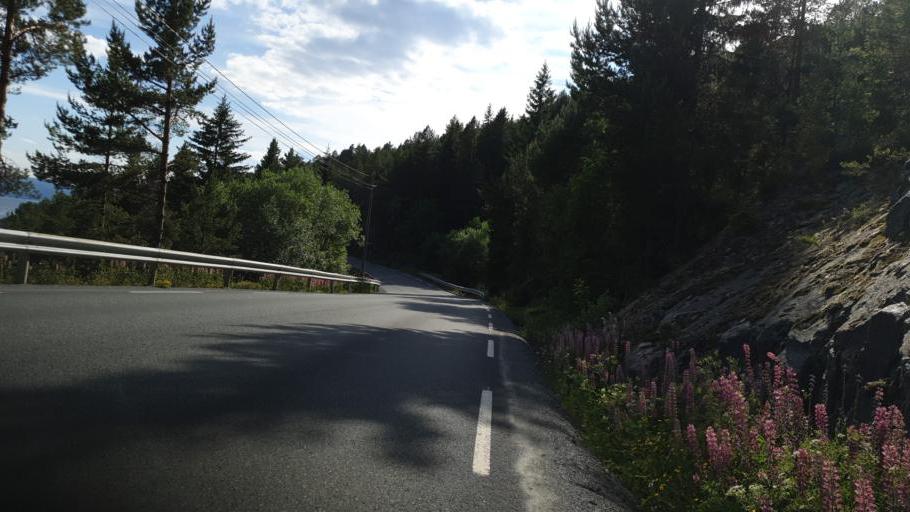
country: NO
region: Sor-Trondelag
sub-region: Trondheim
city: Trondheim
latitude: 63.5705
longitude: 10.3452
